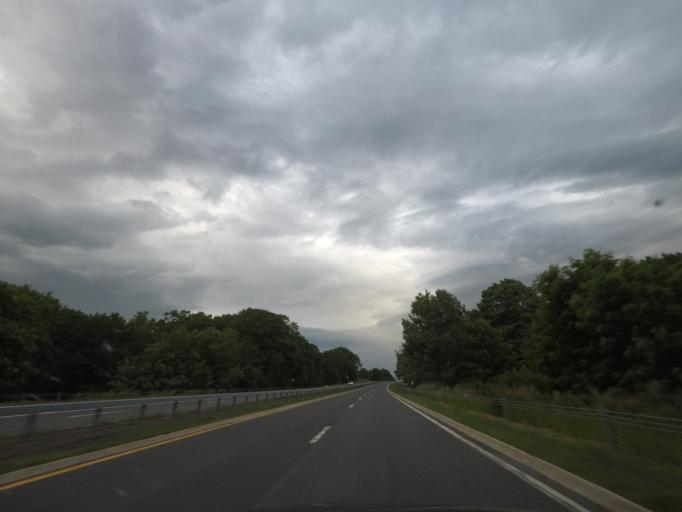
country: US
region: New York
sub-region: Columbia County
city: Philmont
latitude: 42.2107
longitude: -73.6364
